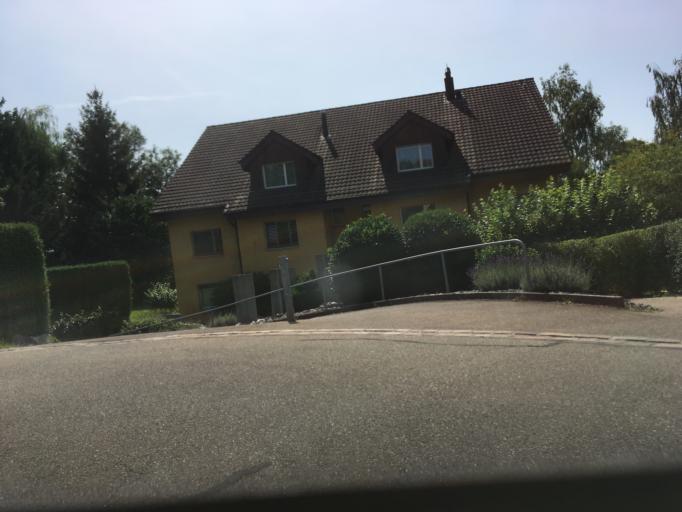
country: CH
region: Zurich
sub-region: Bezirk Buelach
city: Dietlikon / Dietlikon (Dorf)
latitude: 47.4152
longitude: 8.6130
